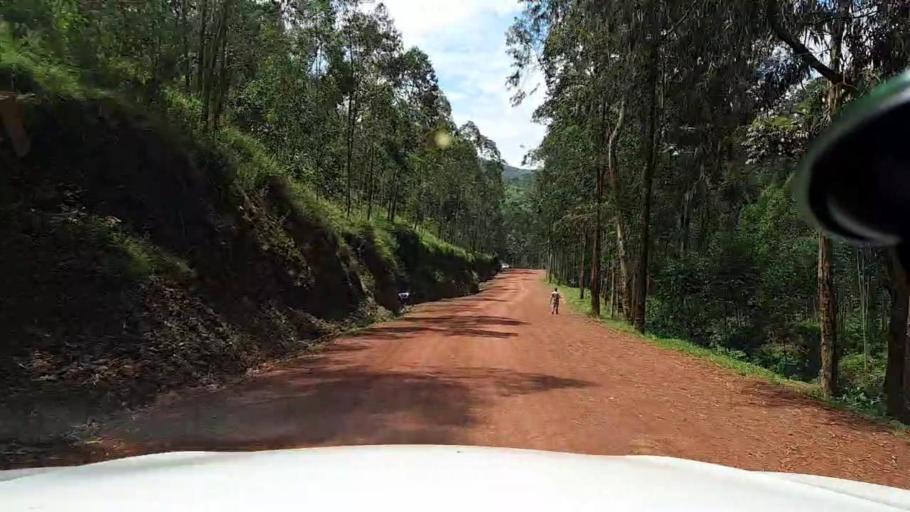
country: RW
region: Northern Province
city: Byumba
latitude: -1.7046
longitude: 29.8466
